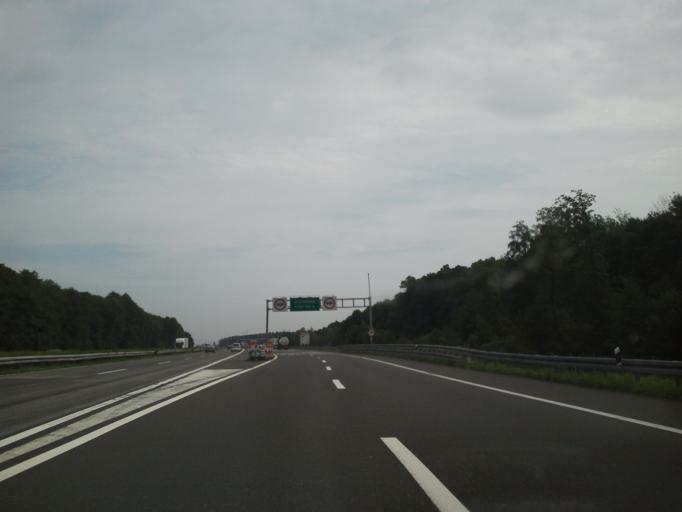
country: HR
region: Grad Zagreb
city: Brezovica
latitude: 45.7173
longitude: 15.8637
